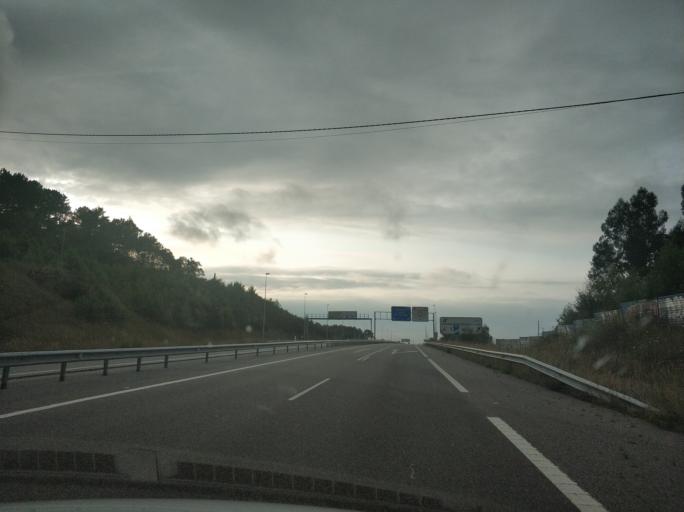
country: ES
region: Asturias
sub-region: Province of Asturias
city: Cudillero
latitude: 43.5516
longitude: -6.1666
